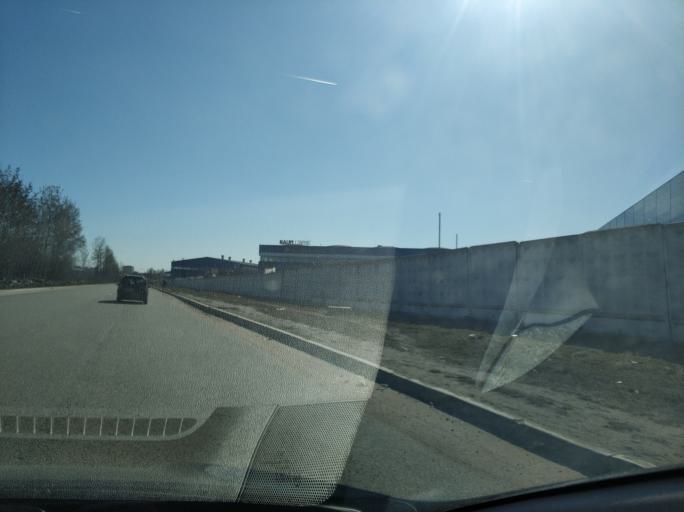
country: RU
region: Leningrad
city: Bugry
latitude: 60.0655
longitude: 30.3830
